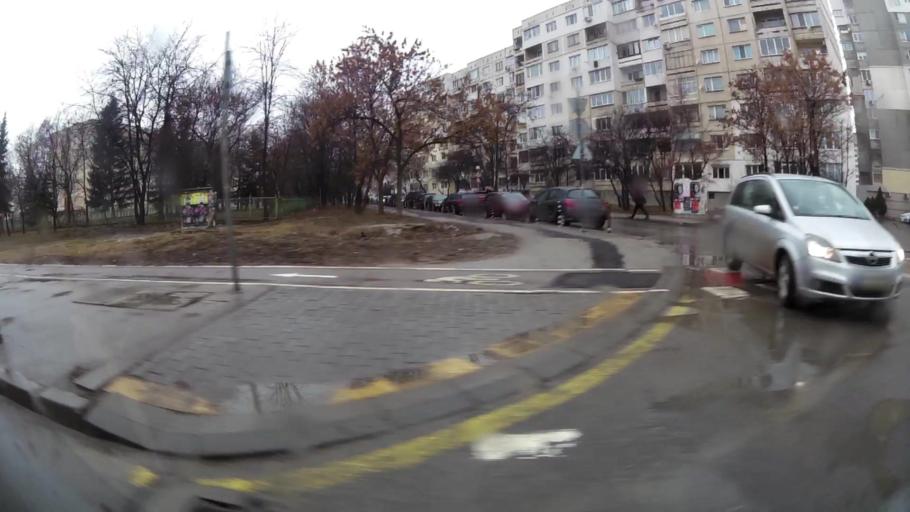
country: BG
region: Sofia-Capital
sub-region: Stolichna Obshtina
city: Sofia
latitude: 42.6439
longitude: 23.3791
